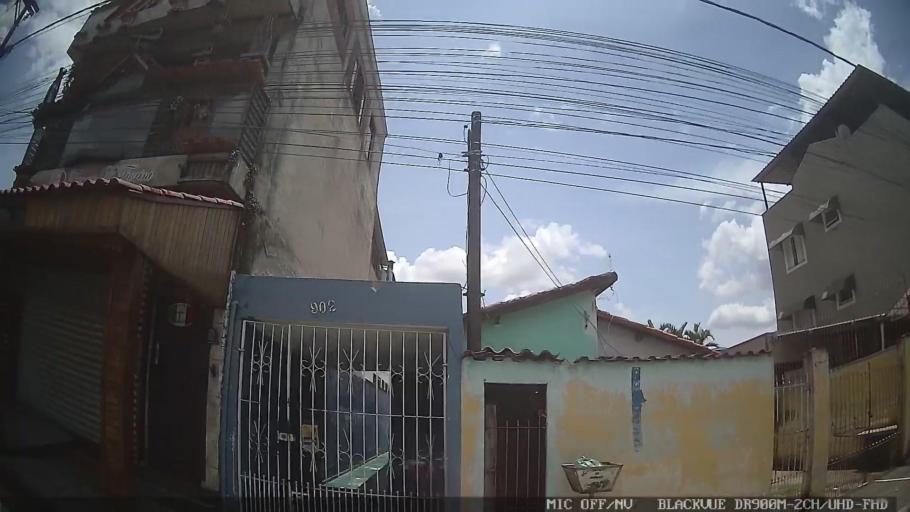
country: BR
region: Sao Paulo
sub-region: Suzano
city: Suzano
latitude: -23.5387
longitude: -46.3214
